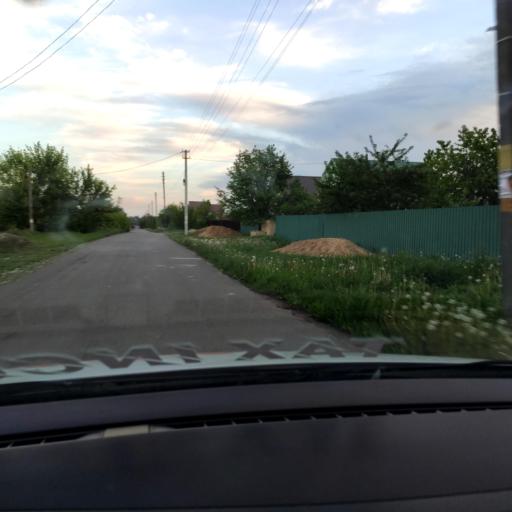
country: RU
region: Voronezj
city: Maslovka
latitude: 51.4443
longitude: 39.2343
